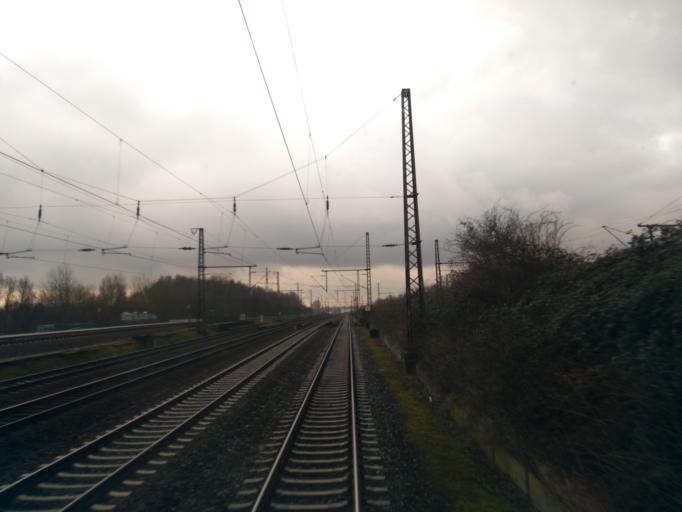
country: DE
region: Hamburg
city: Kleiner Grasbrook
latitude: 53.5176
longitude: 10.0109
